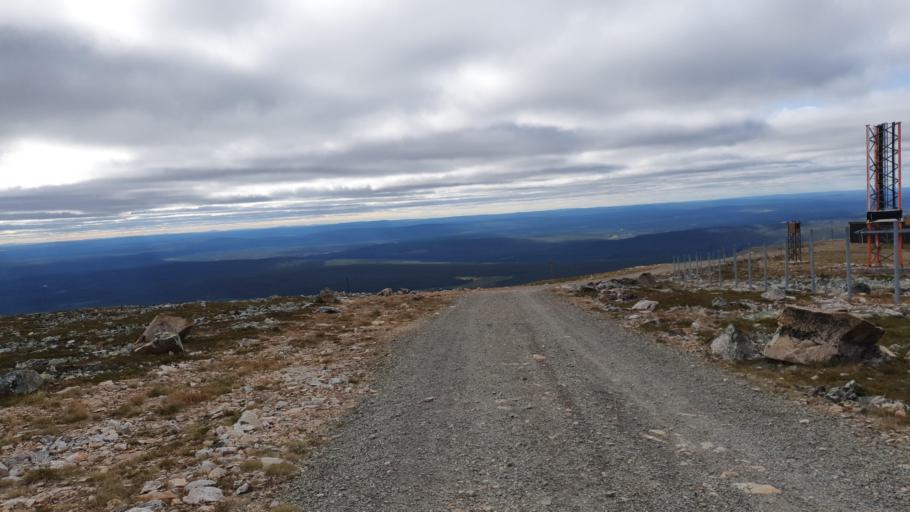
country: FI
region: Lapland
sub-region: Tunturi-Lappi
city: Kolari
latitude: 67.5662
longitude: 24.2119
